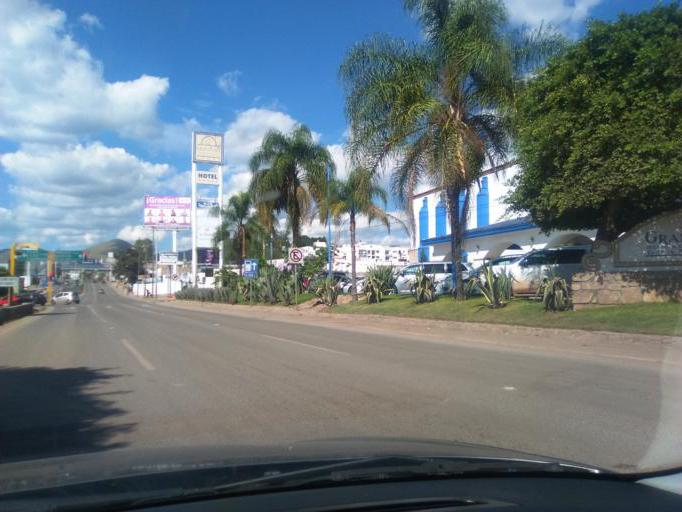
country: MX
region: Guanajuato
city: Marfil
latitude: 20.9868
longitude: -101.2849
